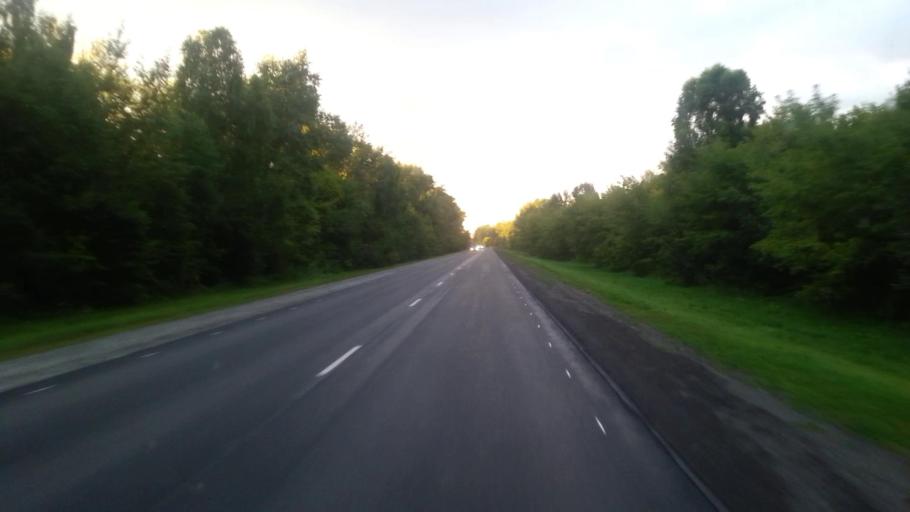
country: RU
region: Altai Krai
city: Berezovka
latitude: 52.3716
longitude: 85.8061
